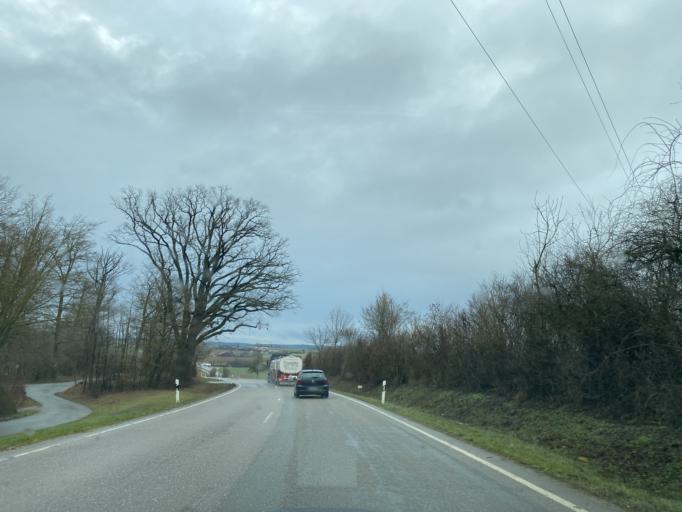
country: DE
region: Baden-Wuerttemberg
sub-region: Regierungsbezirk Stuttgart
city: Hemmingen
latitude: 48.8467
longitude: 8.9977
